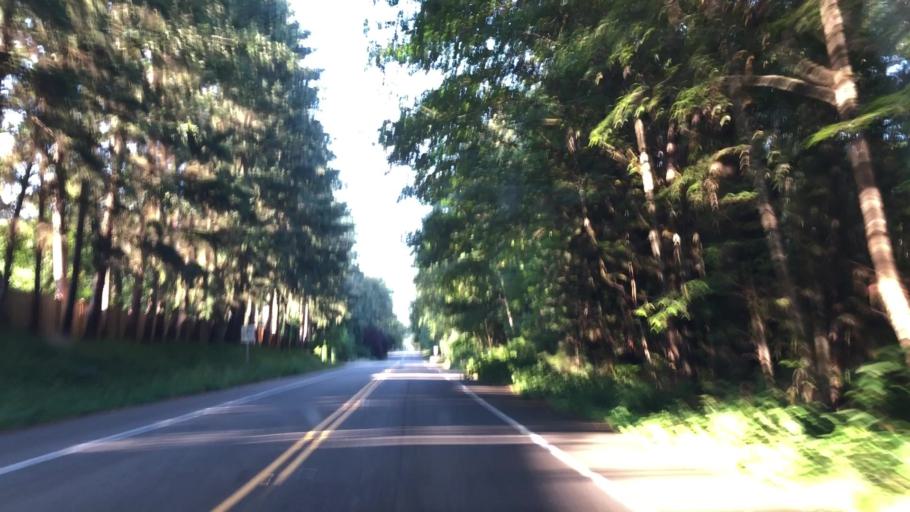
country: US
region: Washington
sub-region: King County
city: Cottage Lake
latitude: 47.7214
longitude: -122.1104
